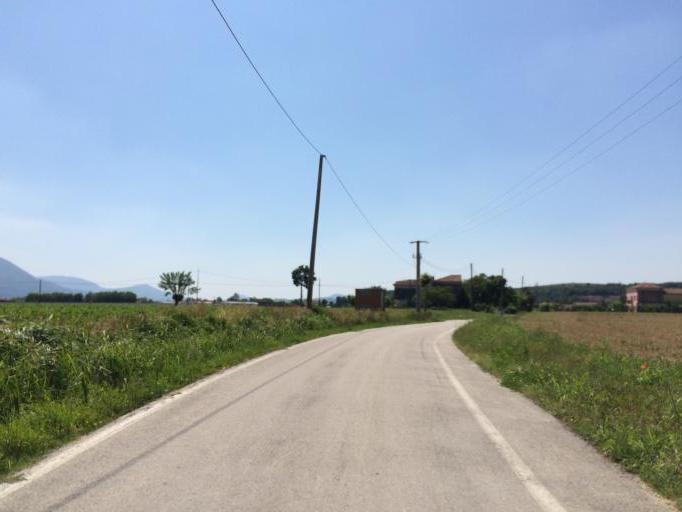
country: IT
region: Veneto
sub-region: Provincia di Vicenza
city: Ponte di Nanto
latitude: 45.4100
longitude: 11.5962
